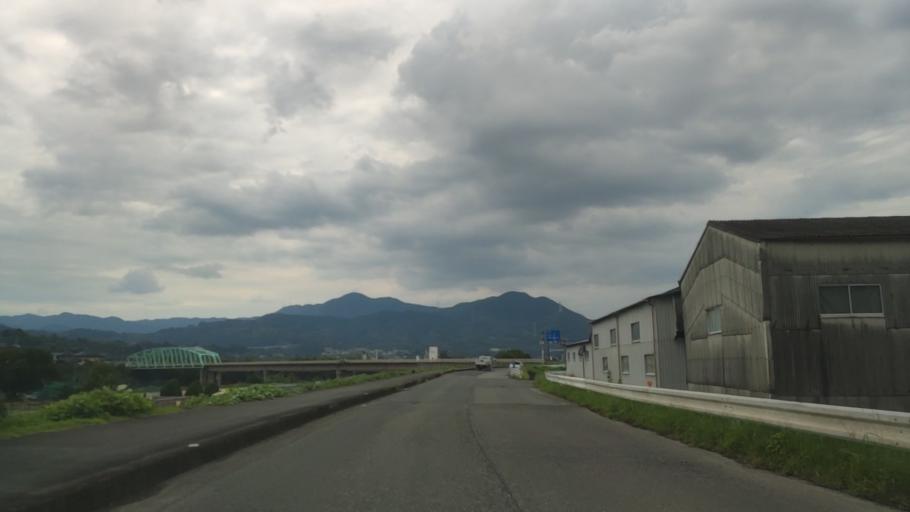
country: JP
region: Wakayama
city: Hashimoto
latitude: 34.3011
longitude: 135.5803
